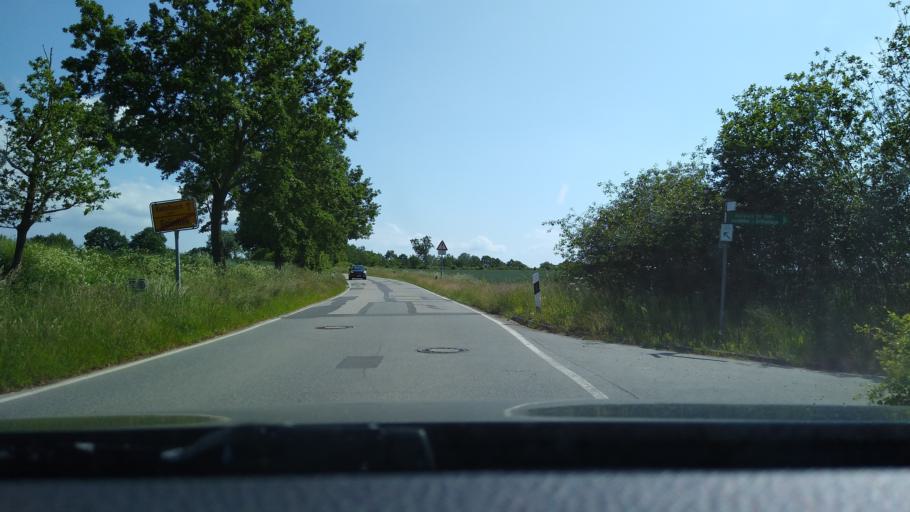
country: DE
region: Schleswig-Holstein
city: Kabelhorst
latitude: 54.2214
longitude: 10.9317
